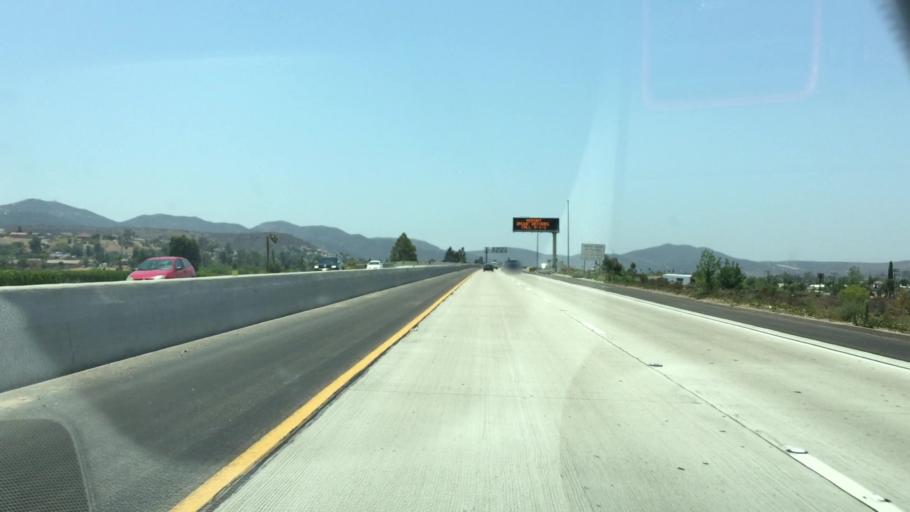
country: US
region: California
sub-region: San Diego County
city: Santee
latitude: 32.8329
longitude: -116.9808
